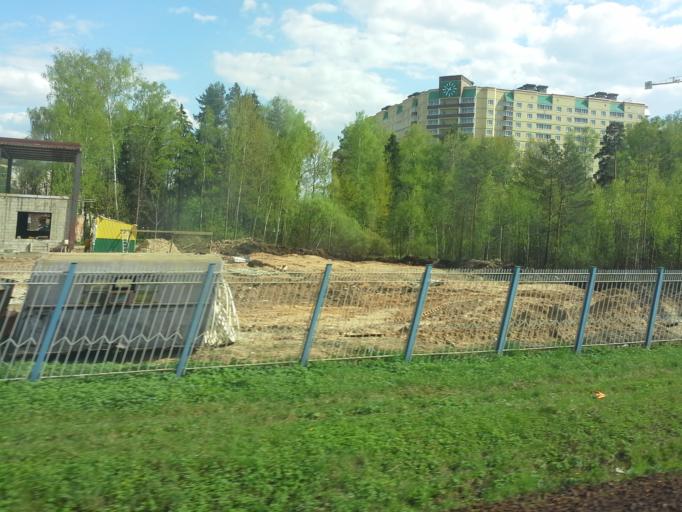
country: RU
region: Moskovskaya
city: Zelenogradskiy
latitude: 56.0927
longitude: 37.8981
